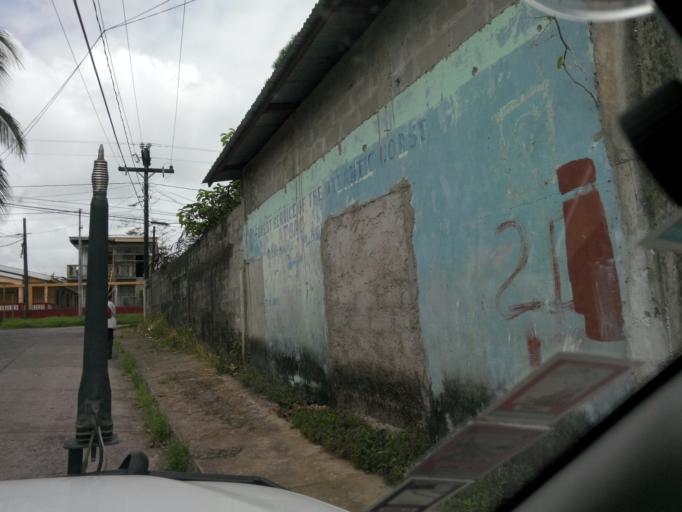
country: NI
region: Atlantico Sur
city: Bluefields
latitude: 12.0180
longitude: -83.7632
